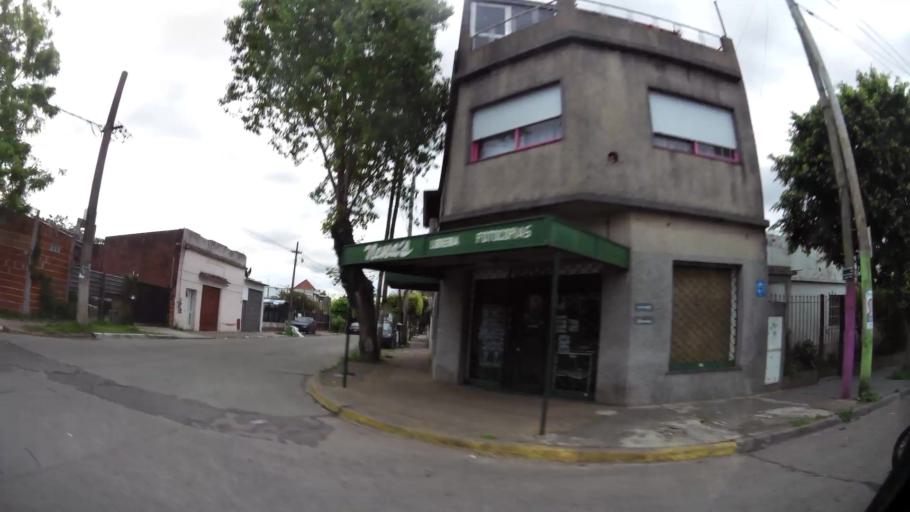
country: AR
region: Buenos Aires
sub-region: Partido de Quilmes
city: Quilmes
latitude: -34.7506
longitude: -58.2310
